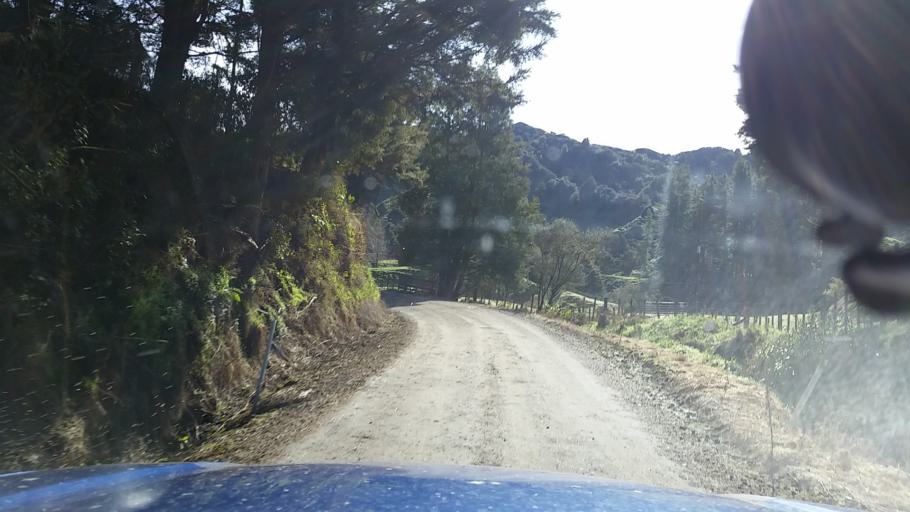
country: NZ
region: Taranaki
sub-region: New Plymouth District
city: Waitara
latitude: -39.0513
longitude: 174.7677
